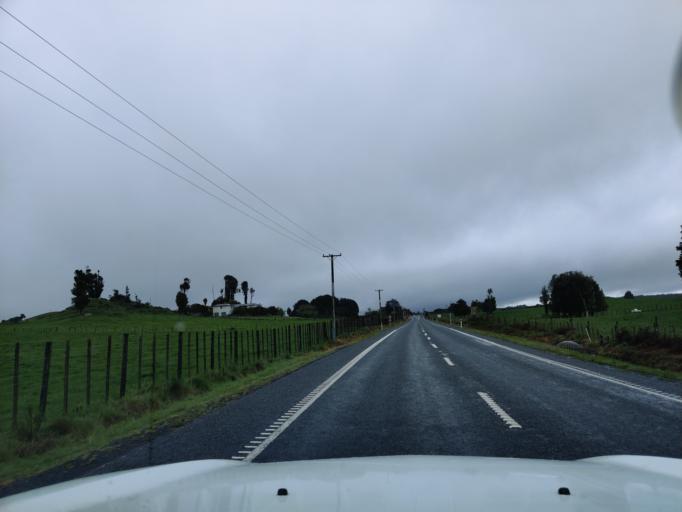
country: NZ
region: Bay of Plenty
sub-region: Rotorua District
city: Rotorua
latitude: -38.0532
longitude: 176.0817
